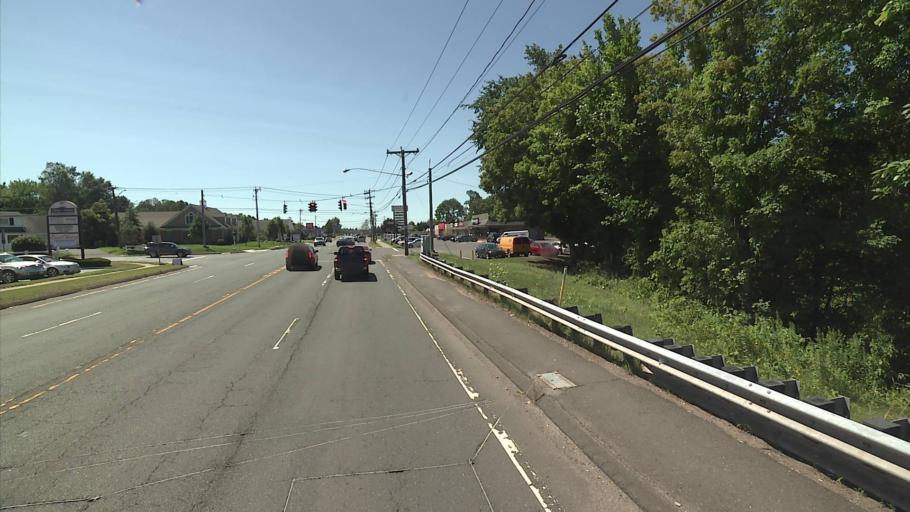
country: US
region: Connecticut
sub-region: Hartford County
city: Plainville
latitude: 41.6439
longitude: -72.8741
